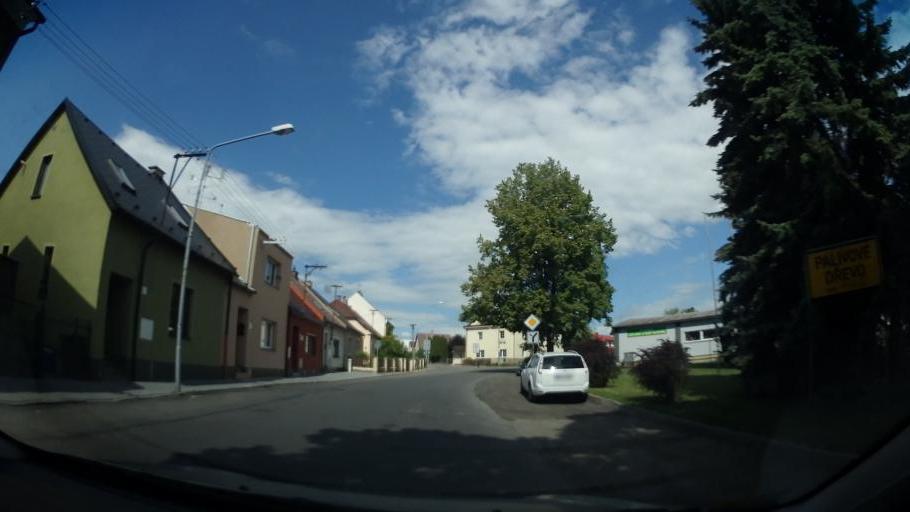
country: CZ
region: Pardubicky
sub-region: Okres Svitavy
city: Moravska Trebova
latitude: 49.7607
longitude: 16.6540
